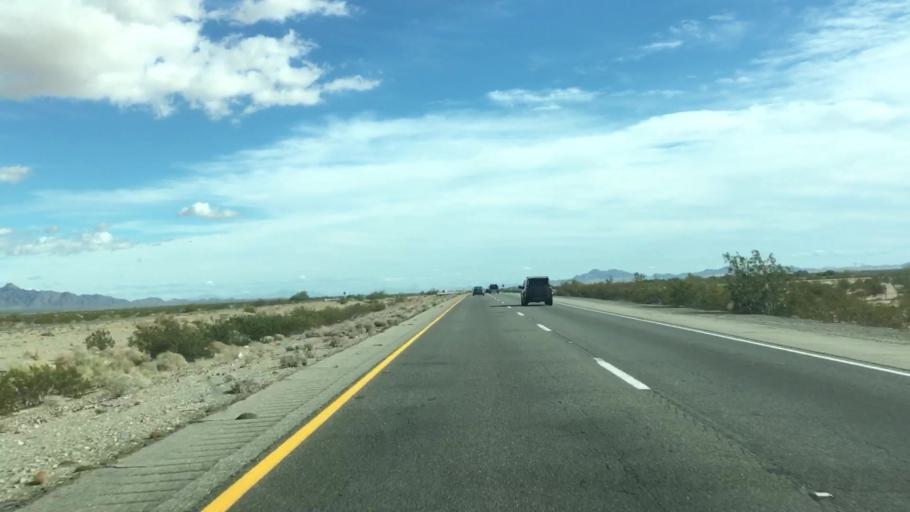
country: US
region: California
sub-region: Riverside County
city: Mesa Verde
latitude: 33.6221
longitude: -115.0411
